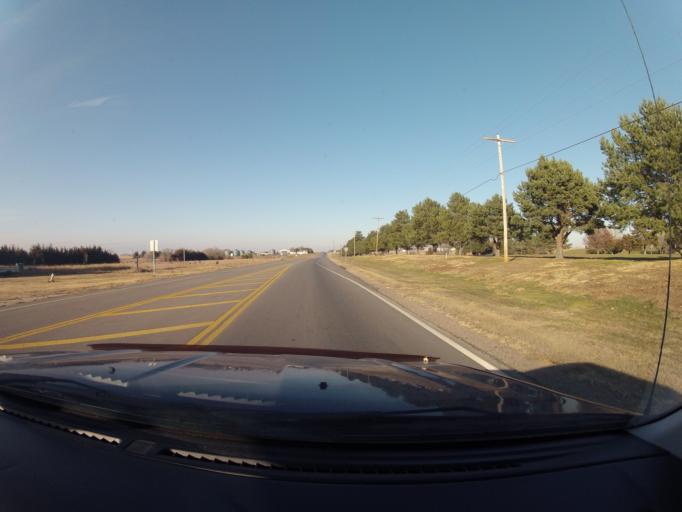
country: US
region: Nebraska
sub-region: Kearney County
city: Minden
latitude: 40.5108
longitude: -98.9518
